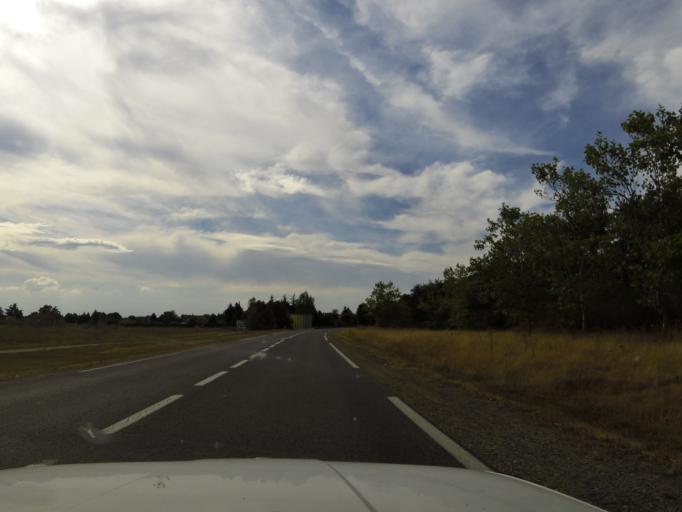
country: FR
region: Rhone-Alpes
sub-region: Departement de l'Ain
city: Saint-Jean-de-Niost
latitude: 45.8443
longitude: 5.2579
